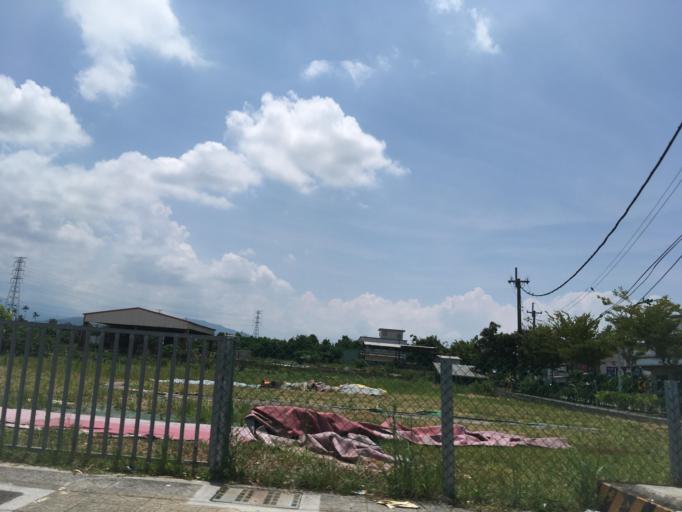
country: TW
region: Taiwan
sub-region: Yilan
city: Yilan
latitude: 24.6624
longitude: 121.7609
